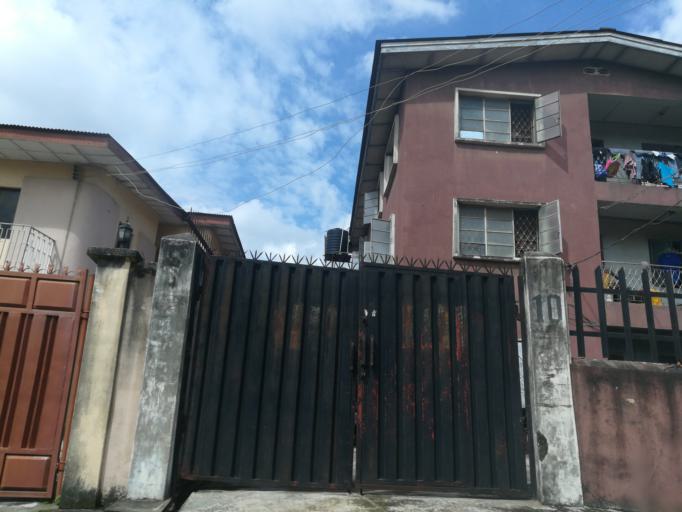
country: NG
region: Lagos
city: Somolu
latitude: 6.5488
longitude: 3.3740
